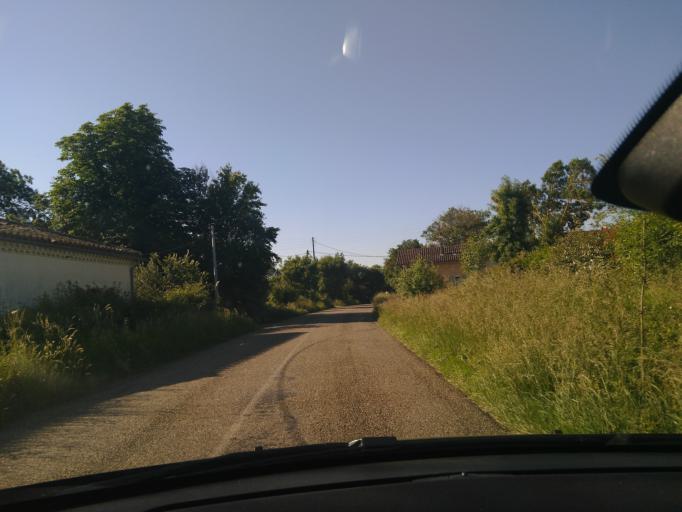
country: FR
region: Midi-Pyrenees
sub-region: Departement du Gers
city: Gimont
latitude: 43.6702
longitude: 0.8932
